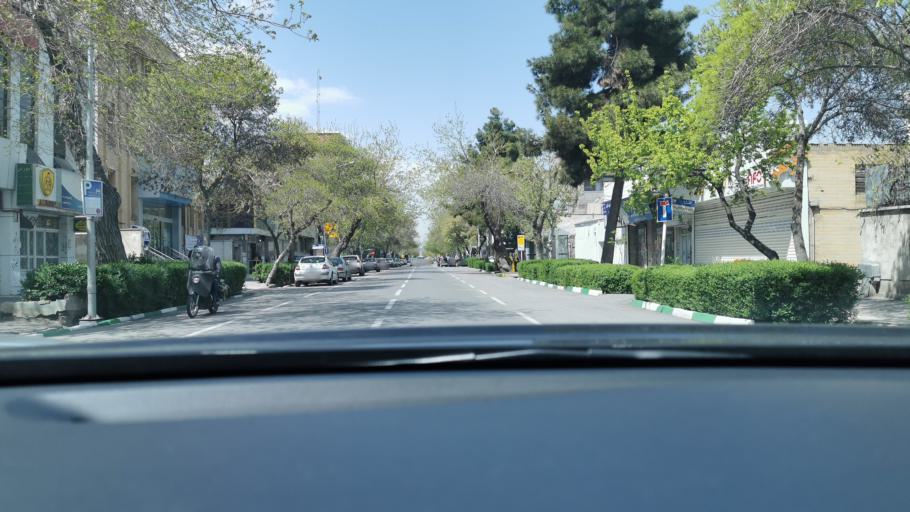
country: IR
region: Razavi Khorasan
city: Mashhad
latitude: 36.2978
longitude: 59.5934
